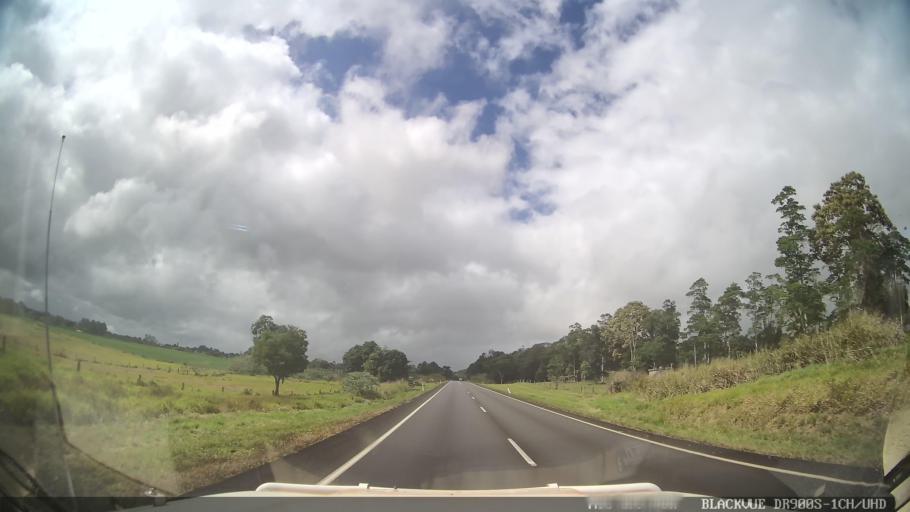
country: AU
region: Queensland
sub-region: Tablelands
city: Atherton
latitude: -17.3031
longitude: 145.6226
